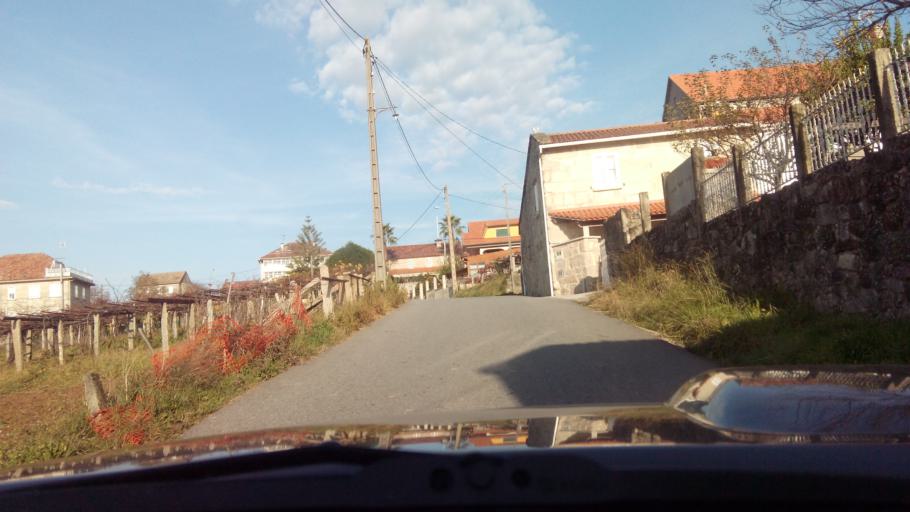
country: ES
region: Galicia
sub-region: Provincia de Pontevedra
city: Marin
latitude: 42.3680
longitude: -8.7278
